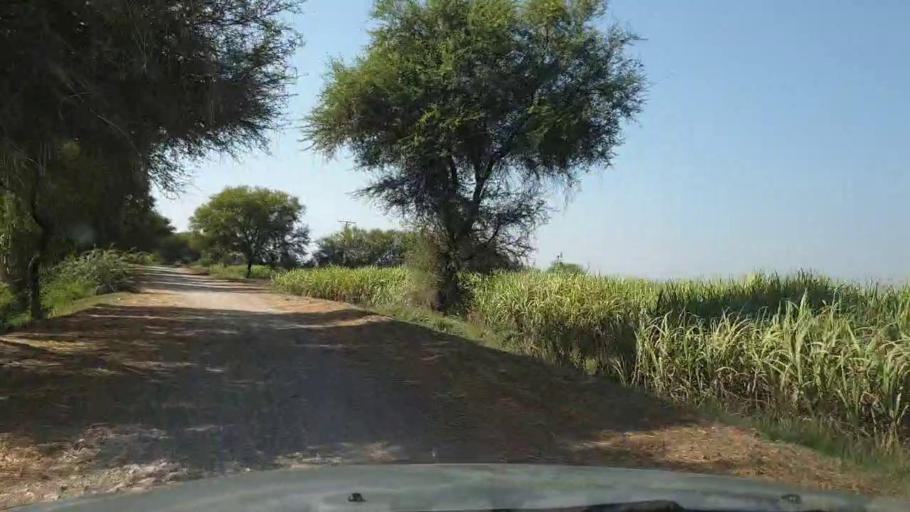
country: PK
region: Sindh
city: Bulri
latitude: 24.9527
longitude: 68.3205
